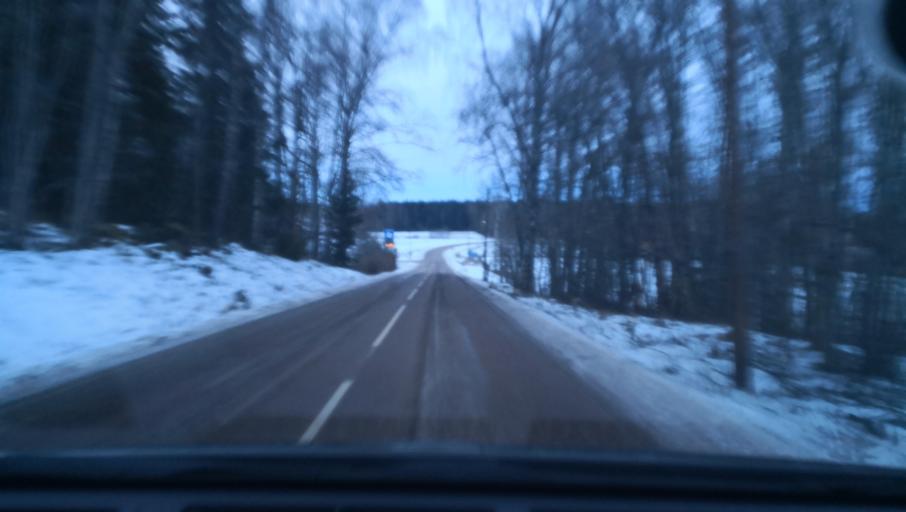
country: SE
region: Dalarna
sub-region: Avesta Kommun
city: Horndal
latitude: 60.1958
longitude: 16.4640
